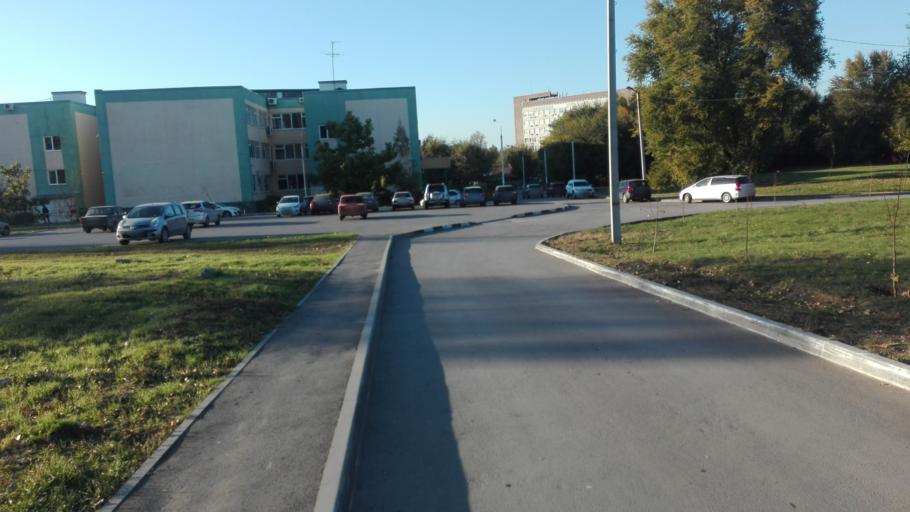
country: RU
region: Rostov
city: Rostov-na-Donu
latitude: 47.2160
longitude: 39.6299
